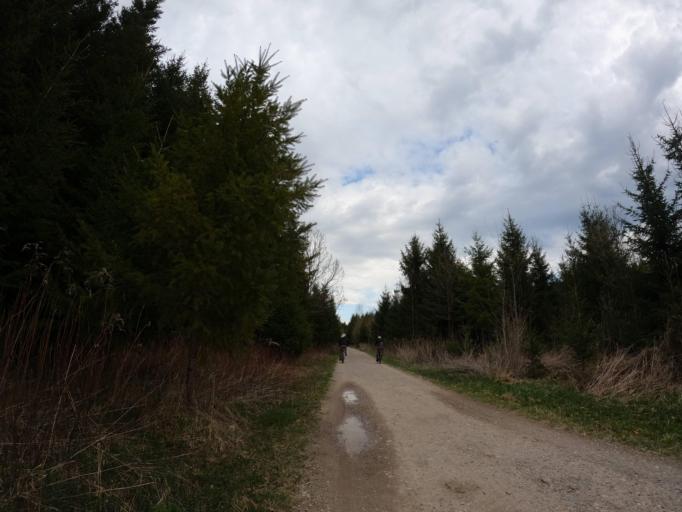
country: DE
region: Bavaria
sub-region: Upper Bavaria
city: Putzbrunn
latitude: 48.0953
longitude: 11.6994
